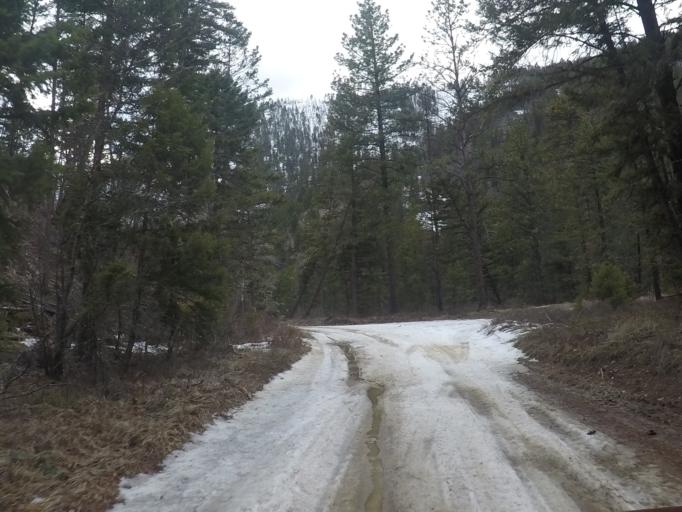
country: US
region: Montana
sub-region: Missoula County
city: Clinton
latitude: 46.5689
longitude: -113.6974
